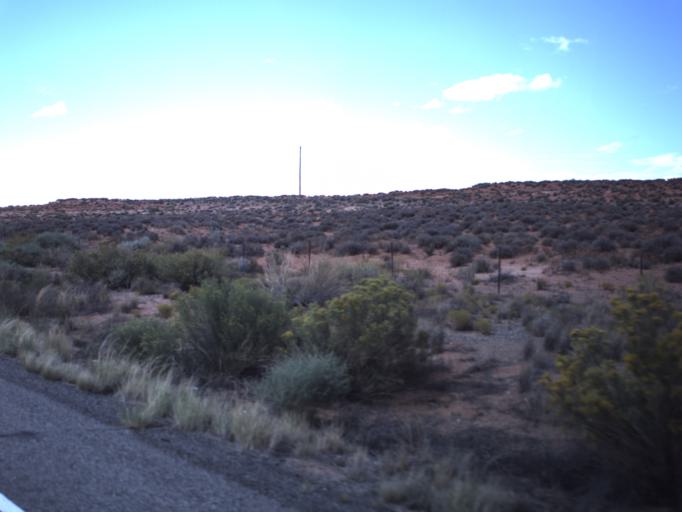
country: US
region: Utah
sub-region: San Juan County
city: Blanding
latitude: 37.2645
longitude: -109.6367
